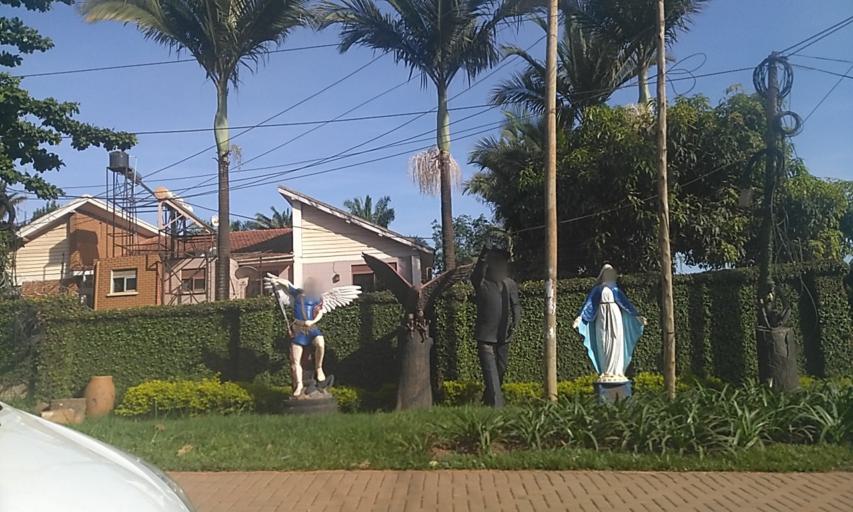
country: UG
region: Central Region
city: Kampala Central Division
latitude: 0.3465
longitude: 32.5973
